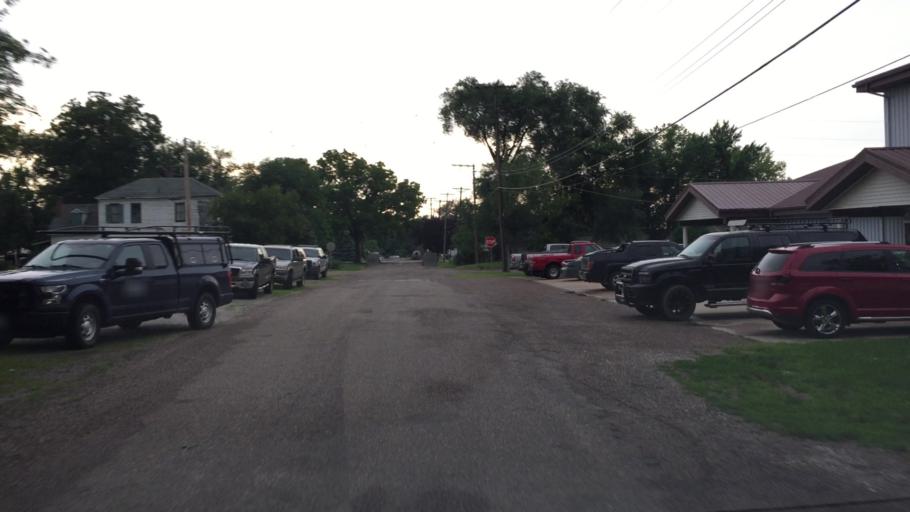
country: US
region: Illinois
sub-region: Hancock County
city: Warsaw
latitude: 40.3580
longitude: -91.4328
